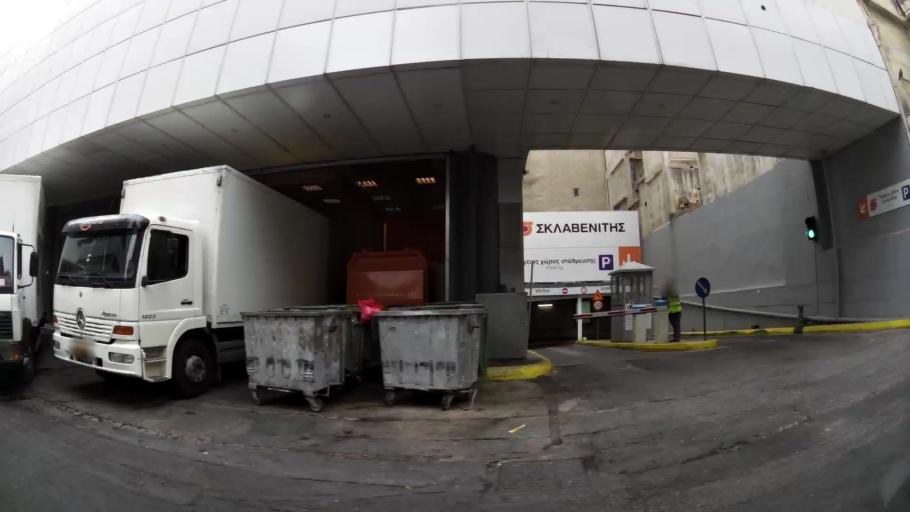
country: GR
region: Attica
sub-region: Nomos Attikis
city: Piraeus
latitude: 37.9398
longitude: 23.6480
